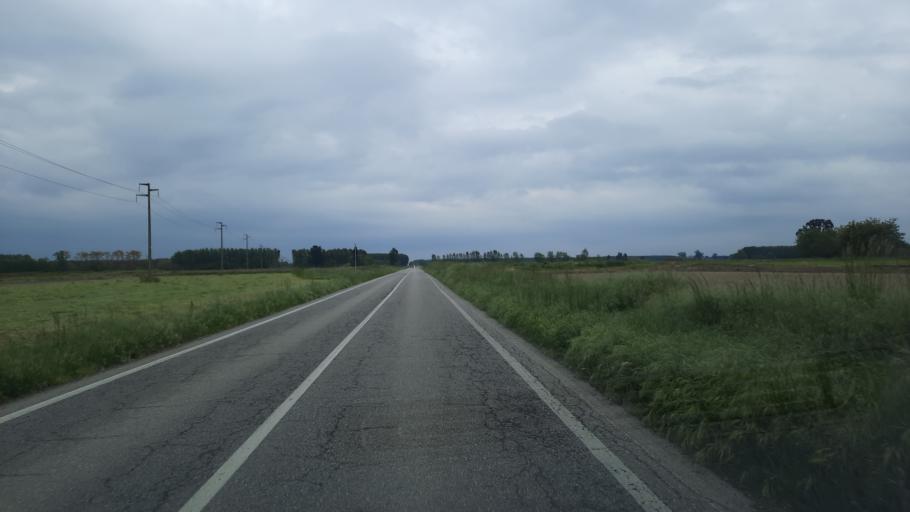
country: IT
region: Lombardy
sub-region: Provincia di Pavia
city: Palestro
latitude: 45.2955
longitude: 8.5522
